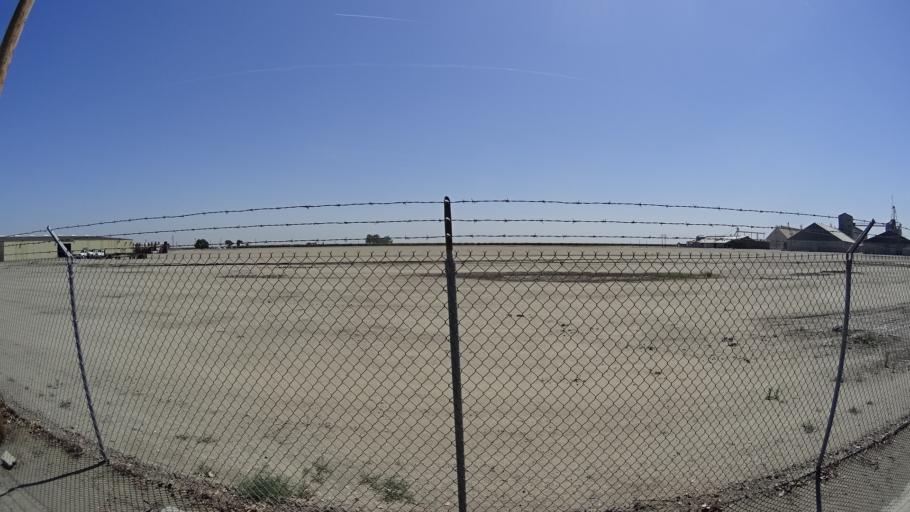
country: US
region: California
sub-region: Kings County
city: Corcoran
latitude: 36.0958
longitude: -119.5543
